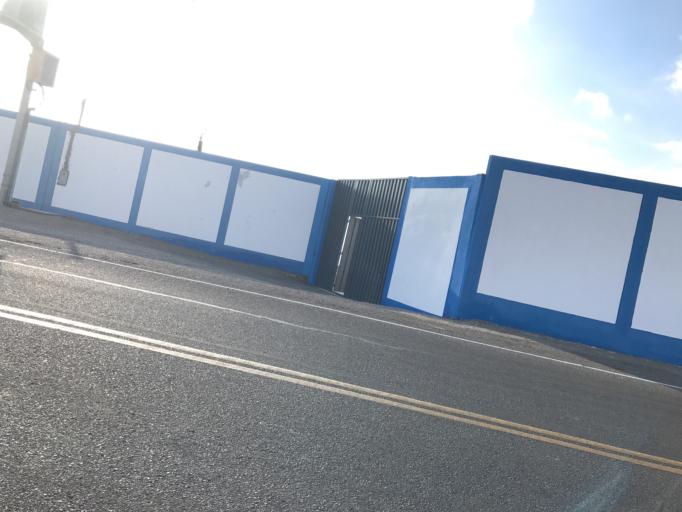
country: PE
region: Moquegua
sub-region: Provincia de Ilo
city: Ilo
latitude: -17.6710
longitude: -71.3619
